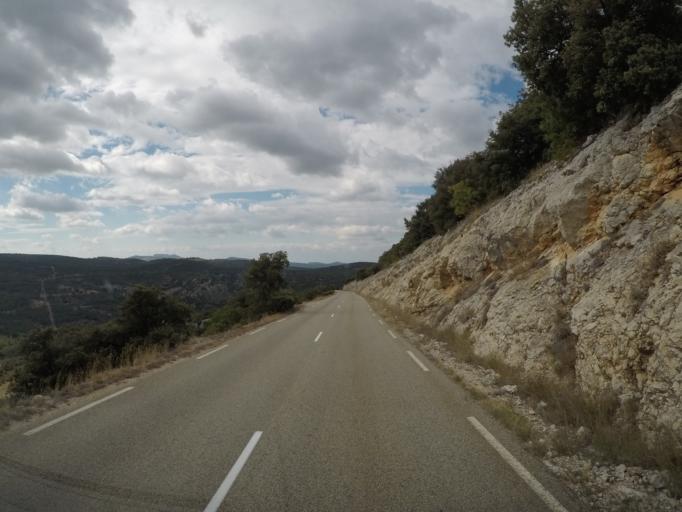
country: FR
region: Rhone-Alpes
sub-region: Departement de la Drome
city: Buis-les-Baronnies
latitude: 44.2218
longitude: 5.2099
